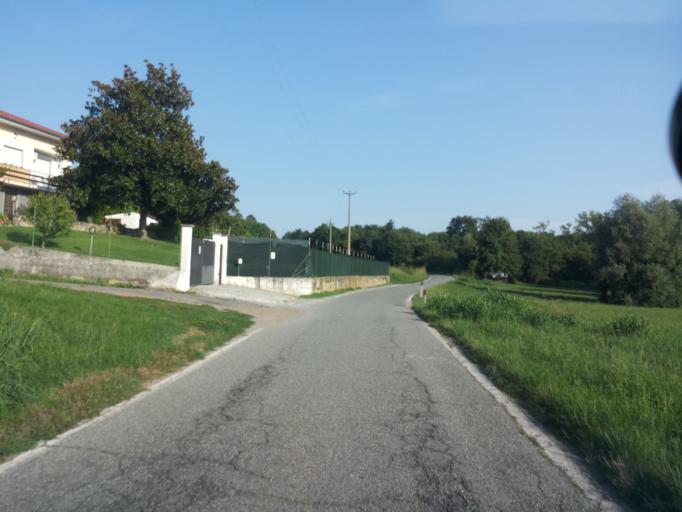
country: IT
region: Piedmont
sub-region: Provincia di Torino
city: Bollengo
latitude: 45.4687
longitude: 7.9575
